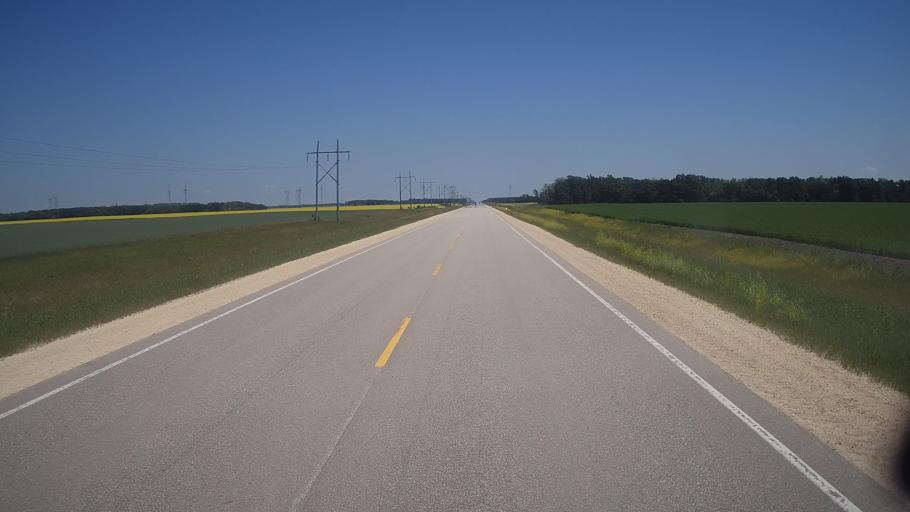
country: CA
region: Manitoba
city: Stonewall
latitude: 50.1227
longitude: -97.5109
